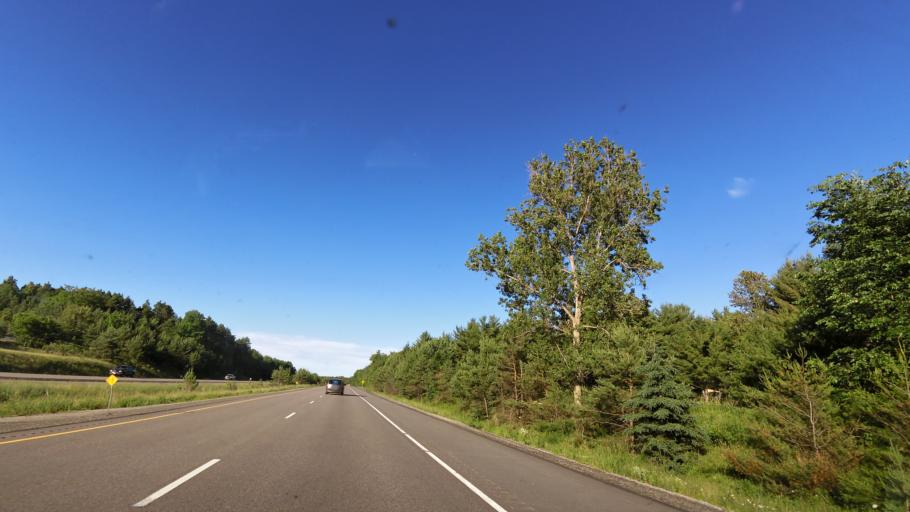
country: CA
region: Ontario
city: Barrie
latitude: 44.5679
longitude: -79.7239
